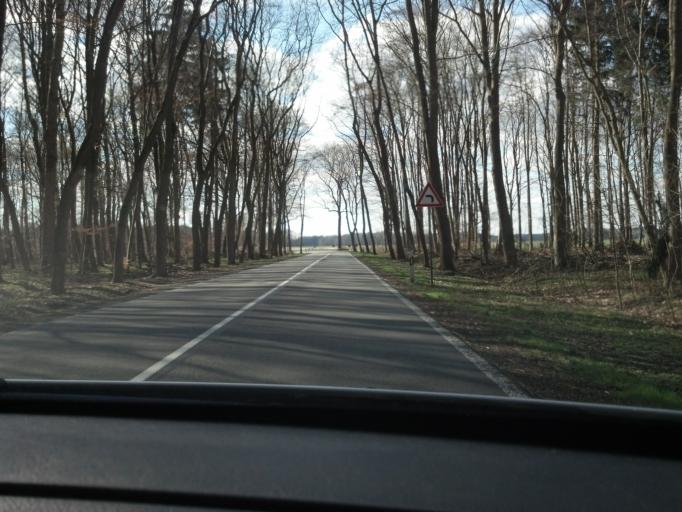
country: DE
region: Brandenburg
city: Gerdshagen
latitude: 53.2863
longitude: 12.1406
